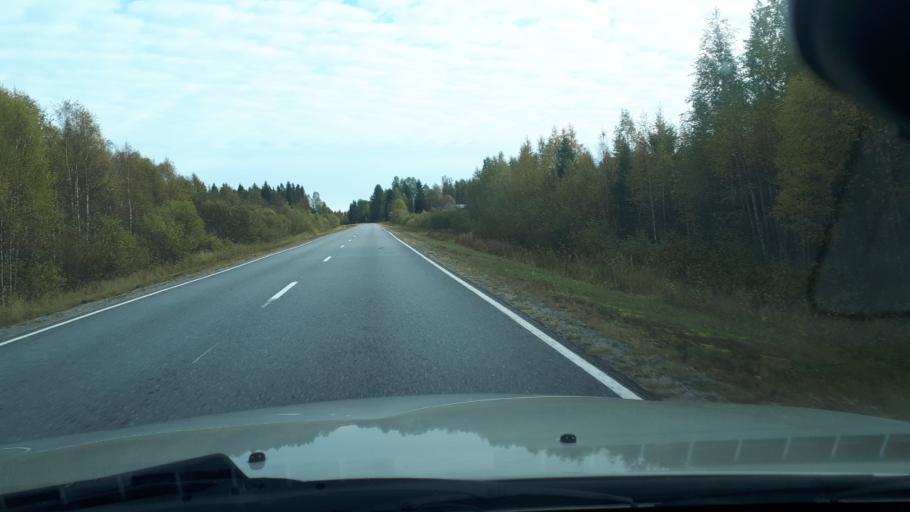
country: FI
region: Lapland
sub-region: Rovaniemi
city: Rovaniemi
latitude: 65.9534
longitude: 25.9230
